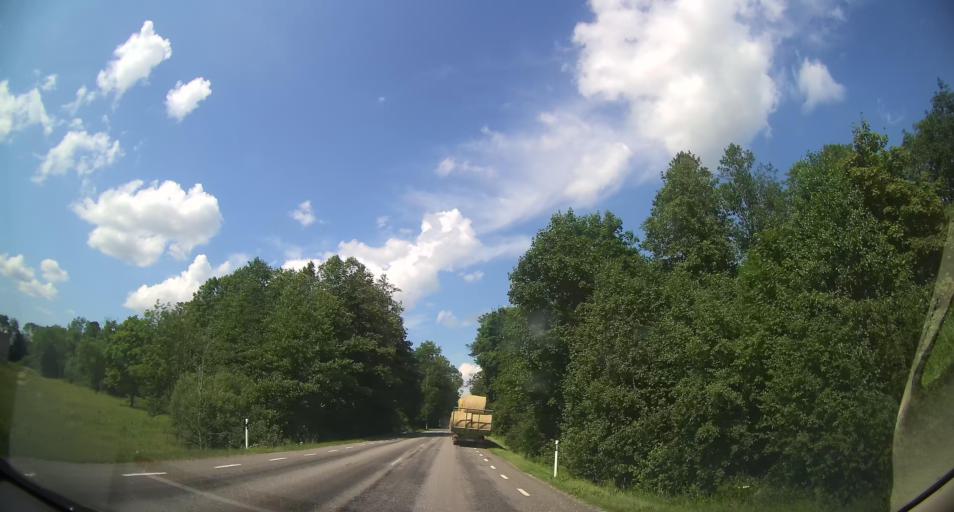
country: EE
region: Raplamaa
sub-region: Maerjamaa vald
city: Marjamaa
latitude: 58.8944
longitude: 24.2436
